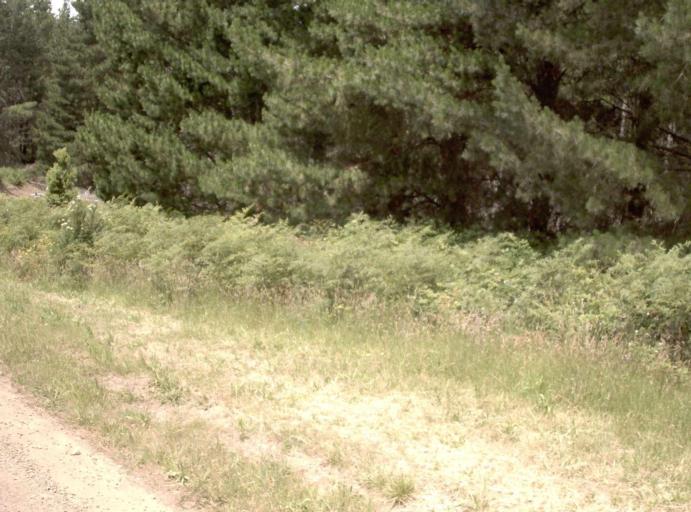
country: AU
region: Victoria
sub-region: Latrobe
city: Traralgon
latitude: -38.4053
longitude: 146.6402
